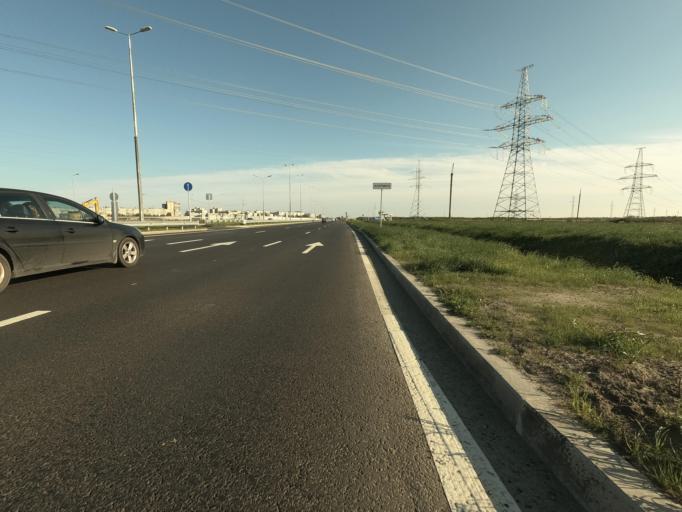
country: RU
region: St.-Petersburg
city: Kolpino
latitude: 59.7411
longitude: 30.5462
